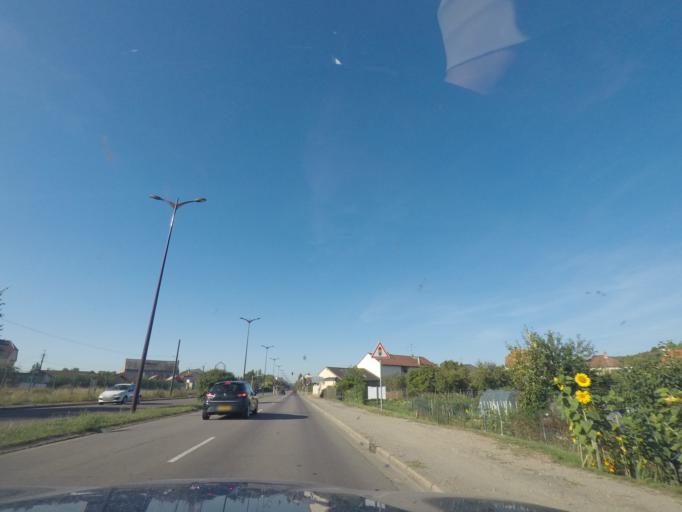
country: FR
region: Lorraine
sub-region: Departement de la Moselle
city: Thionville
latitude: 49.3720
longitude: 6.1651
